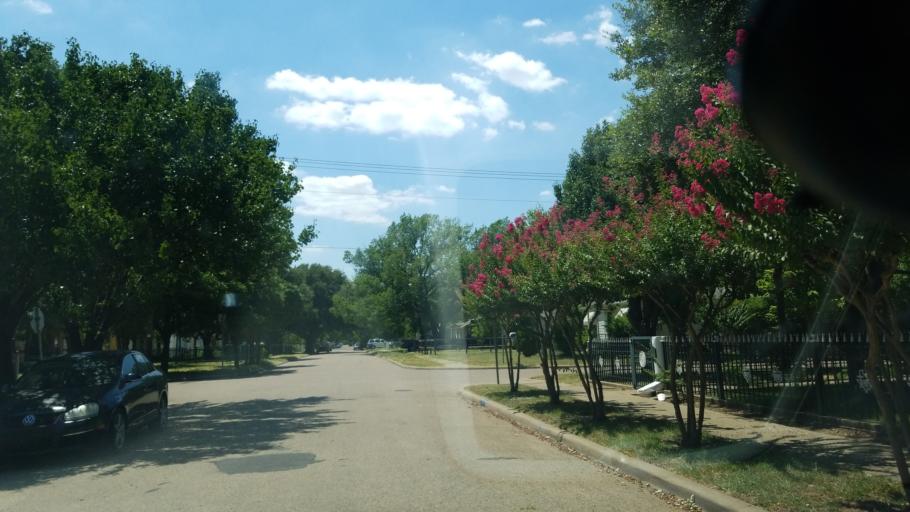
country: US
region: Texas
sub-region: Dallas County
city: Cockrell Hill
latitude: 32.7167
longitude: -96.8457
